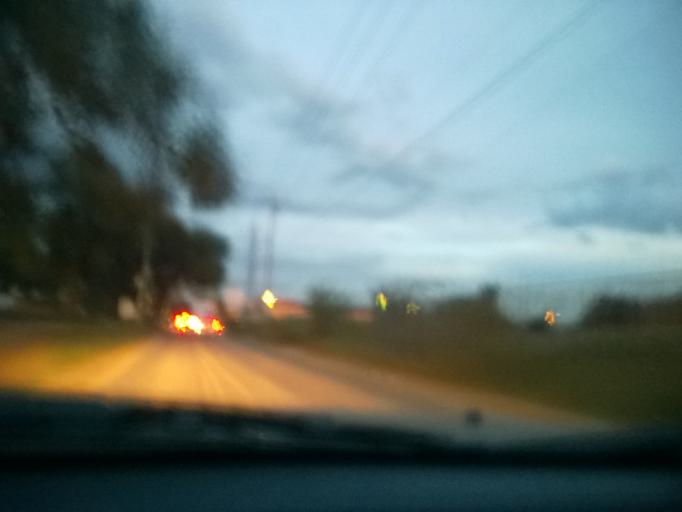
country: MX
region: Guanajuato
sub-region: Leon
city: Fraccionamiento Paraiso Real
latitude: 21.1176
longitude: -101.6099
